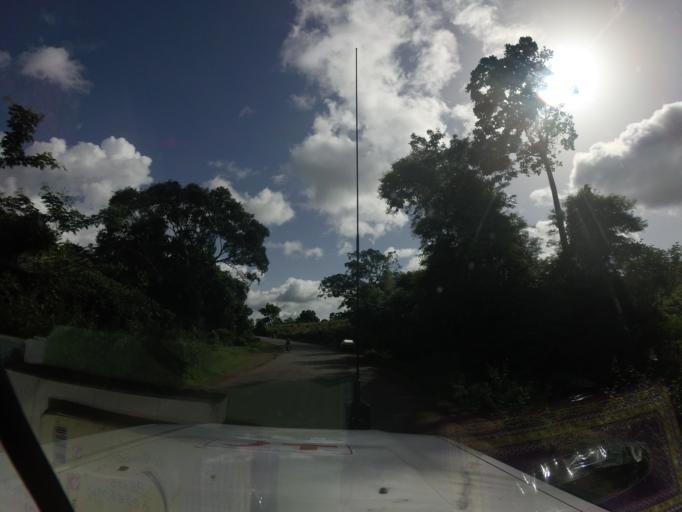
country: GN
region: Mamou
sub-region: Mamou Prefecture
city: Mamou
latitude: 10.3005
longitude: -12.3166
